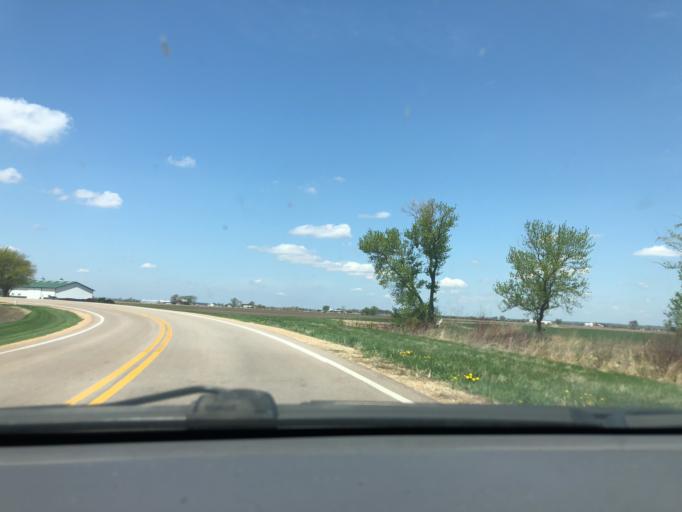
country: US
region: Illinois
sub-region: Kane County
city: Hampshire
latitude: 42.1092
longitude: -88.5580
